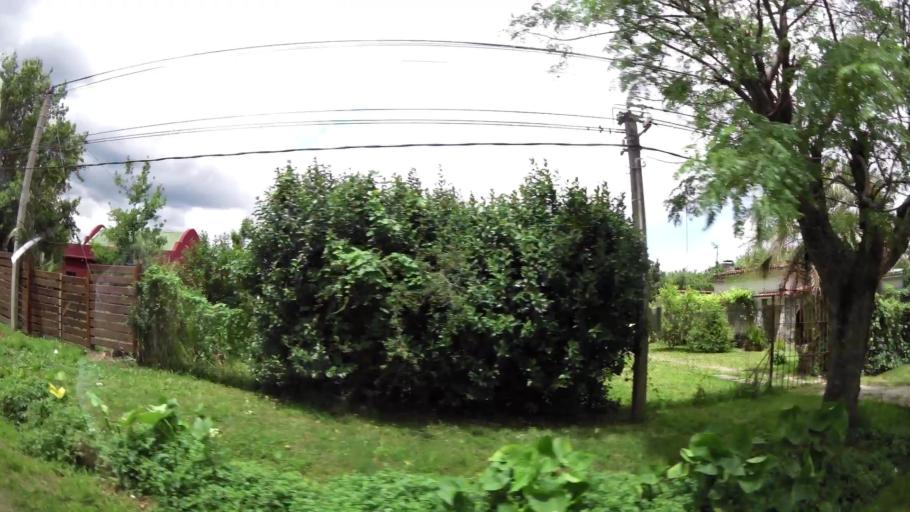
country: UY
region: Canelones
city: Toledo
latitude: -34.8024
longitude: -56.1342
